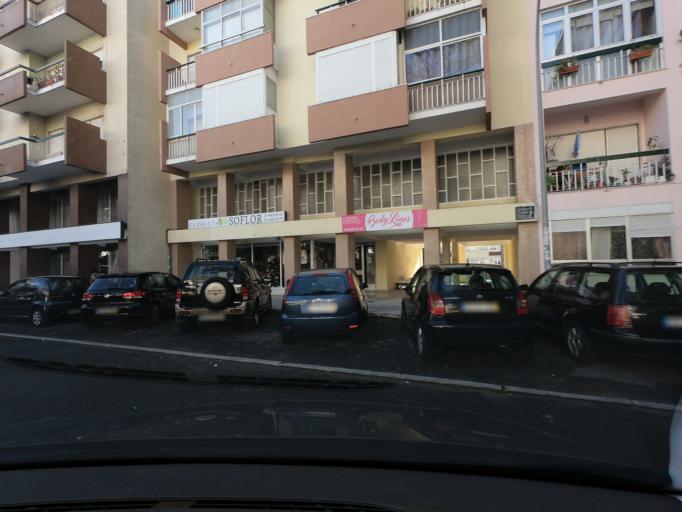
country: PT
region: Lisbon
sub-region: Oeiras
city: Oeiras
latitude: 38.6965
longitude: -9.3040
